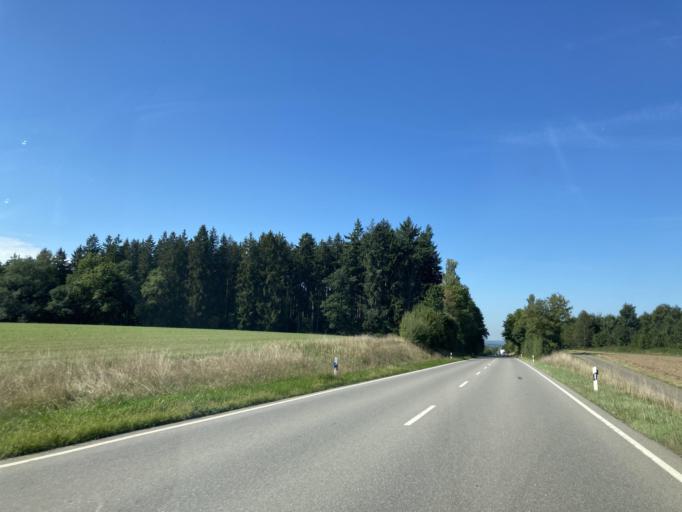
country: DE
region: Baden-Wuerttemberg
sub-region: Tuebingen Region
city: Betzenweiler
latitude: 48.1390
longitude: 9.5623
